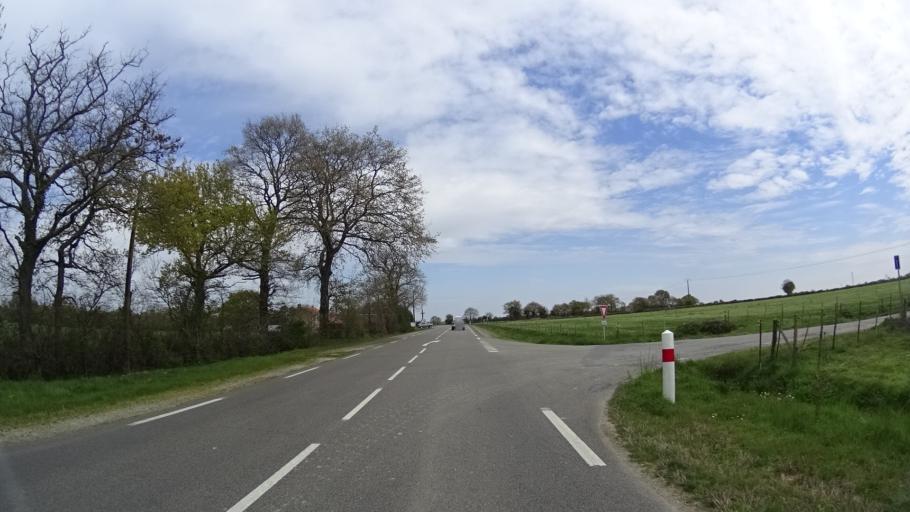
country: FR
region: Pays de la Loire
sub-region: Departement de la Loire-Atlantique
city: Saint-Hilaire-de-Chaleons
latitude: 47.0823
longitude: -1.8629
